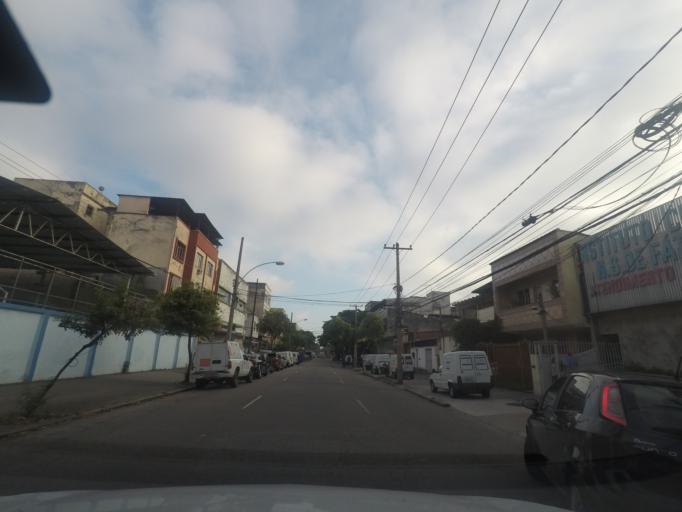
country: BR
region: Rio de Janeiro
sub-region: Duque De Caxias
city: Duque de Caxias
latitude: -22.8376
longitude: -43.2796
